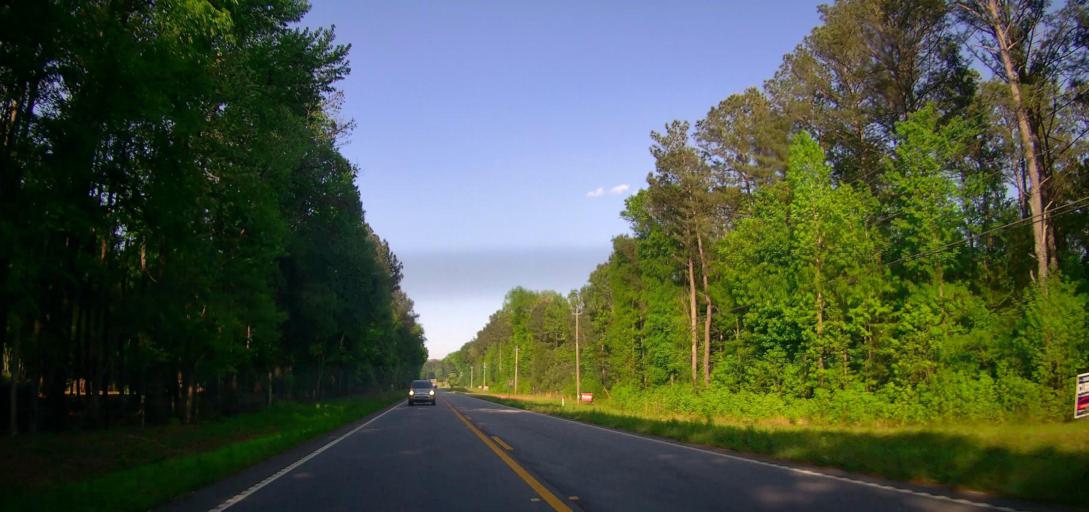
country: US
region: Georgia
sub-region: Newton County
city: Covington
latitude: 33.5942
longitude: -83.7868
